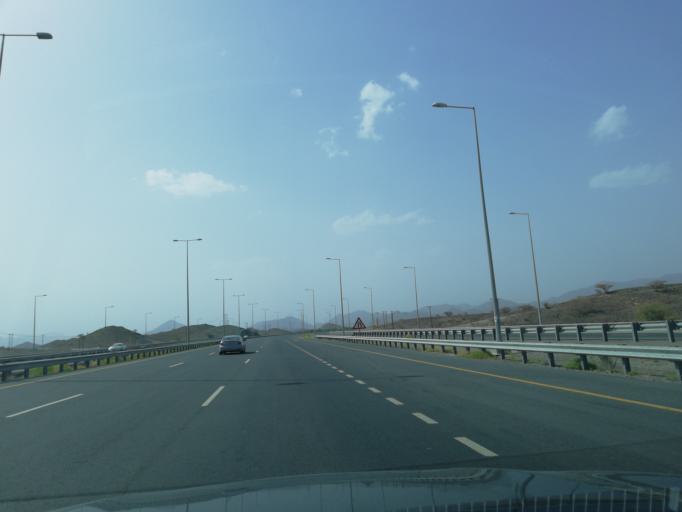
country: OM
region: Muhafazat ad Dakhiliyah
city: Sufalat Sama'il
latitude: 23.0526
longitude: 58.1934
